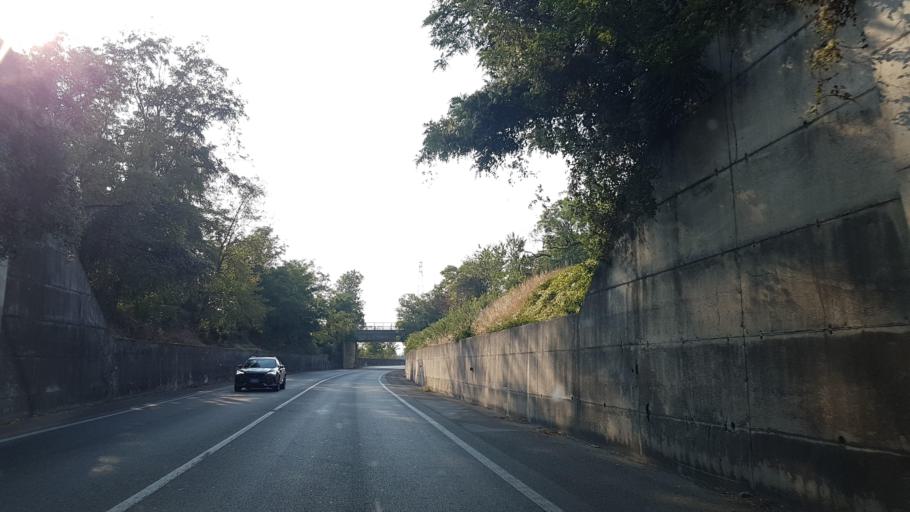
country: IT
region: Emilia-Romagna
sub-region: Provincia di Parma
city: Collecchio
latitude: 44.7573
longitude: 10.2153
